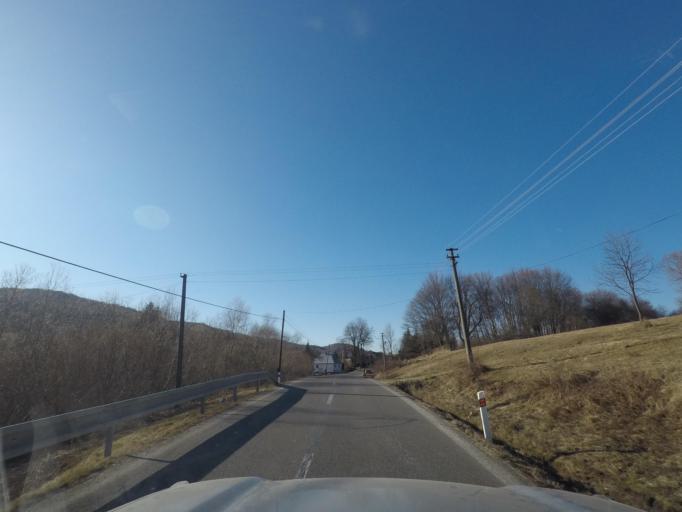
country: SK
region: Presovsky
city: Medzilaborce
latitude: 49.1896
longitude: 22.0079
